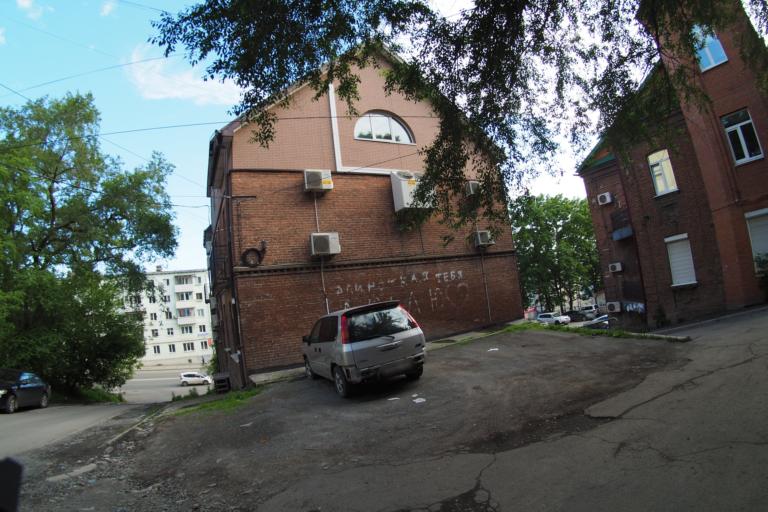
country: RU
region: Primorskiy
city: Vladivostok
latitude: 43.1127
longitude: 131.9212
